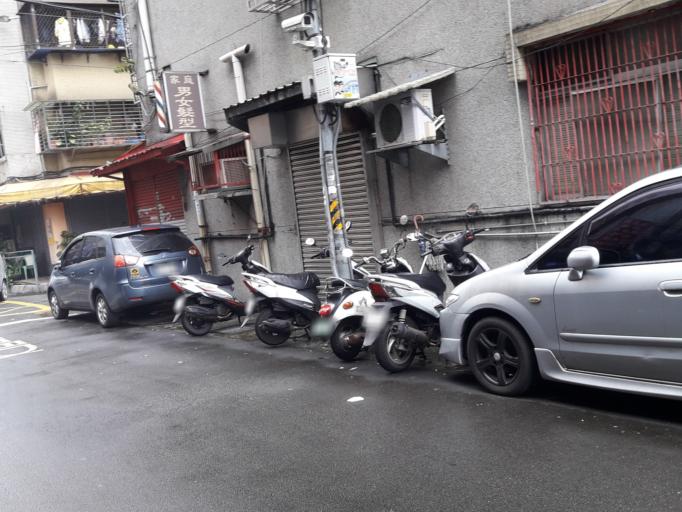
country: TW
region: Taipei
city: Taipei
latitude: 25.0555
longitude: 121.5802
